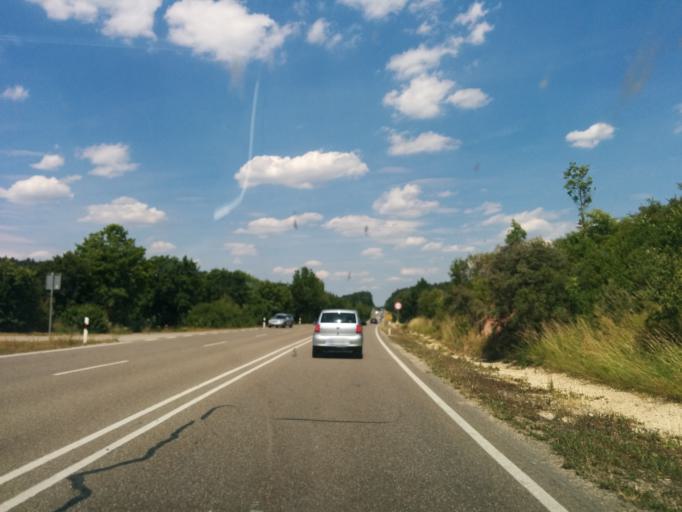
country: DE
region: Bavaria
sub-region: Regierungsbezirk Mittelfranken
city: Ellingen
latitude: 49.0786
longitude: 10.9717
